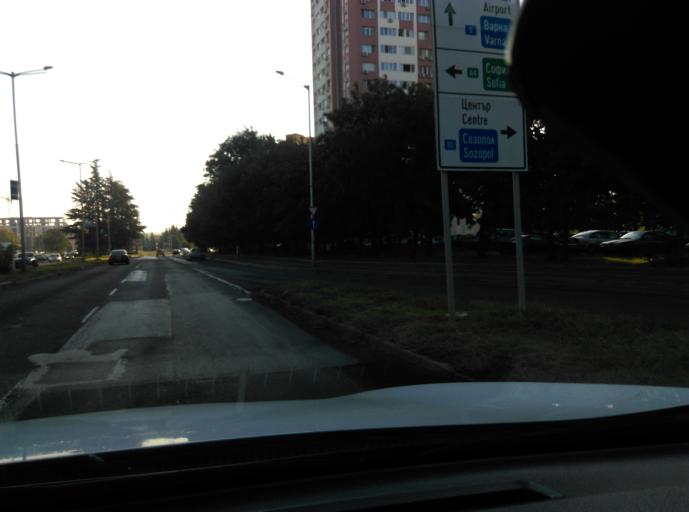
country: BG
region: Burgas
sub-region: Obshtina Burgas
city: Burgas
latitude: 42.5259
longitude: 27.4502
